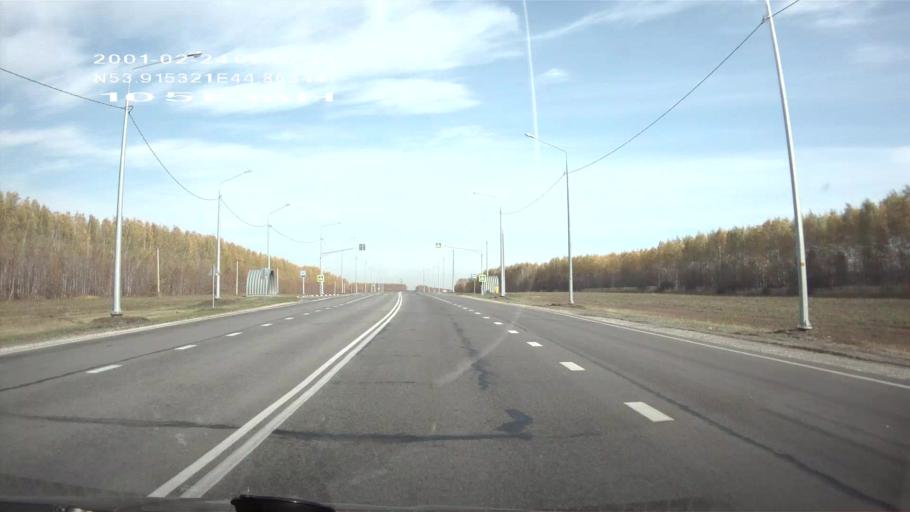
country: RU
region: Penza
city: Issa
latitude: 53.9158
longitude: 44.8643
